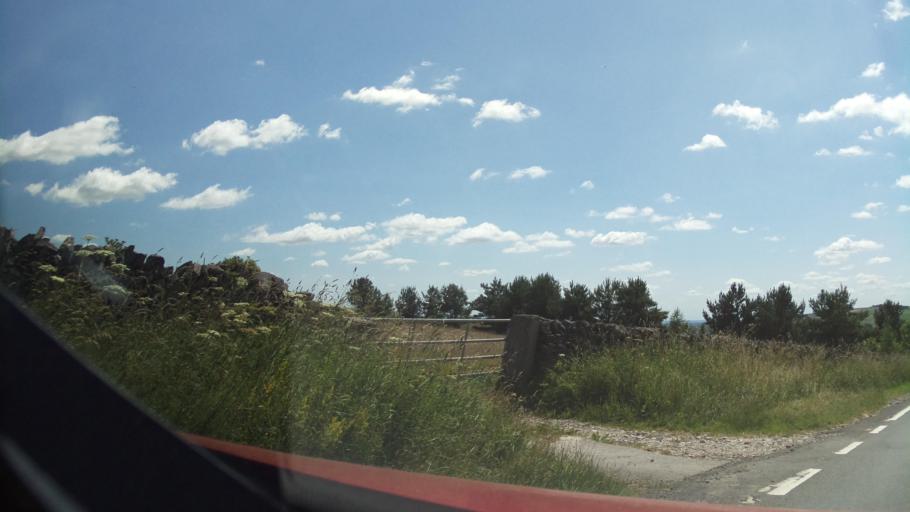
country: GB
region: England
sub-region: Derbyshire
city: Ashbourne
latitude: 53.1092
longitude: -1.7575
